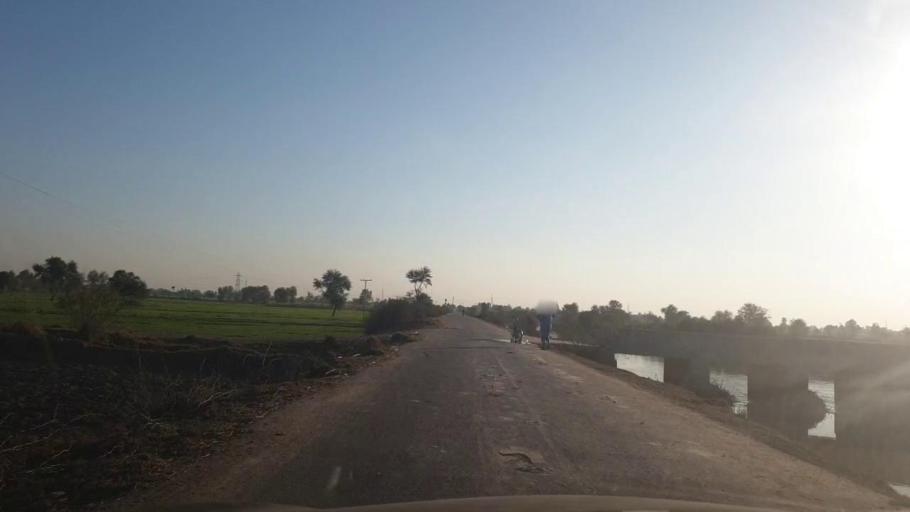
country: PK
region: Sindh
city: Mirpur Mathelo
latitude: 28.0026
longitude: 69.4688
